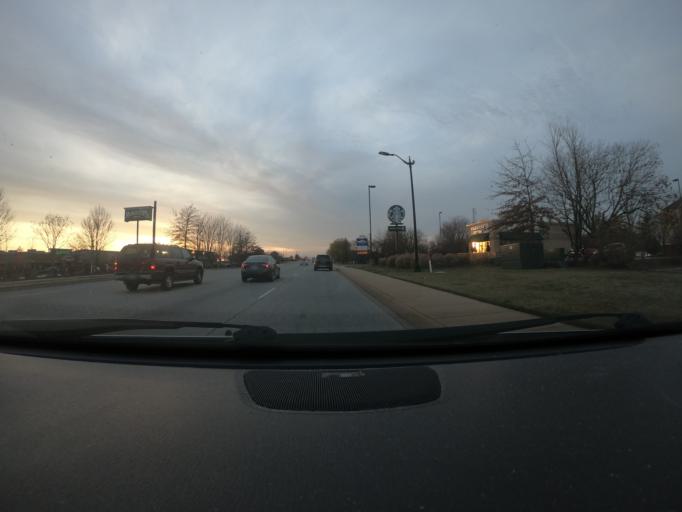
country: US
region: Arkansas
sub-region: Benton County
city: Bentonville
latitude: 36.3354
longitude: -94.1993
